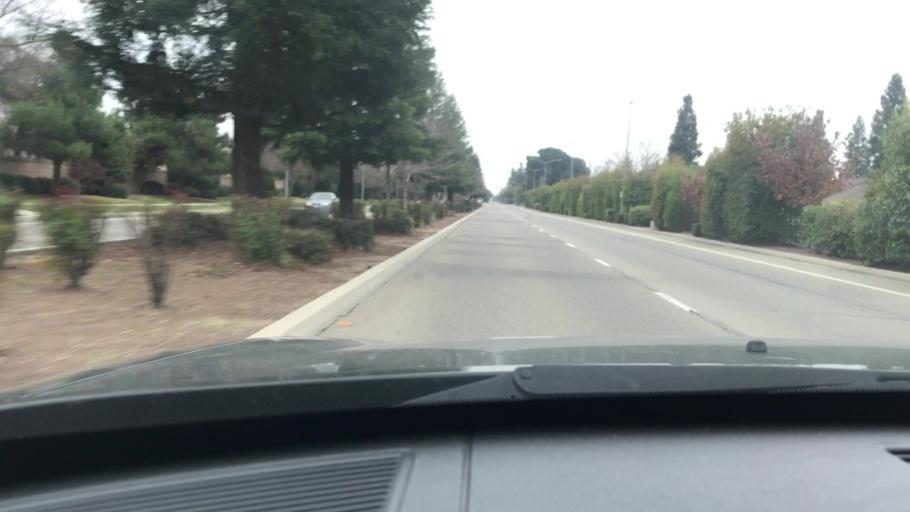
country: US
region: California
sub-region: Fresno County
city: Clovis
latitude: 36.8189
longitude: -119.6639
